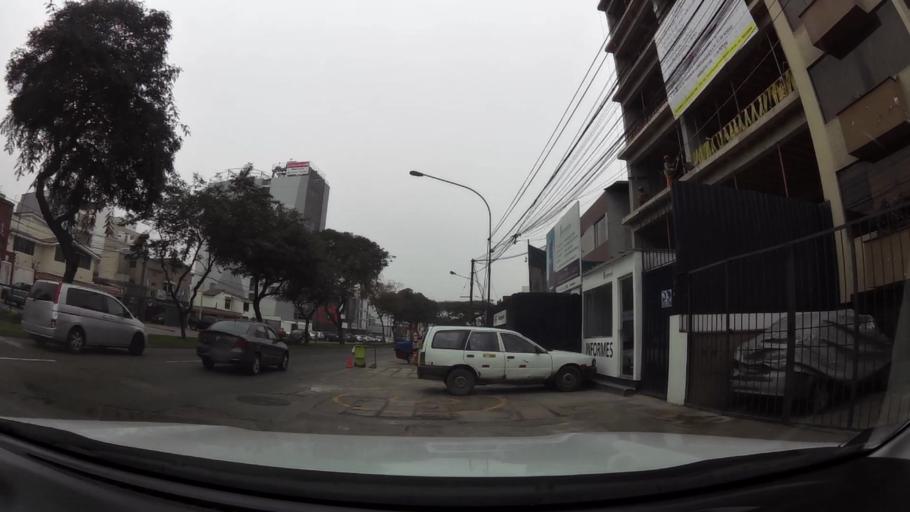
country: PE
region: Lima
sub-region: Lima
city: Surco
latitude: -12.1280
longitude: -76.9872
